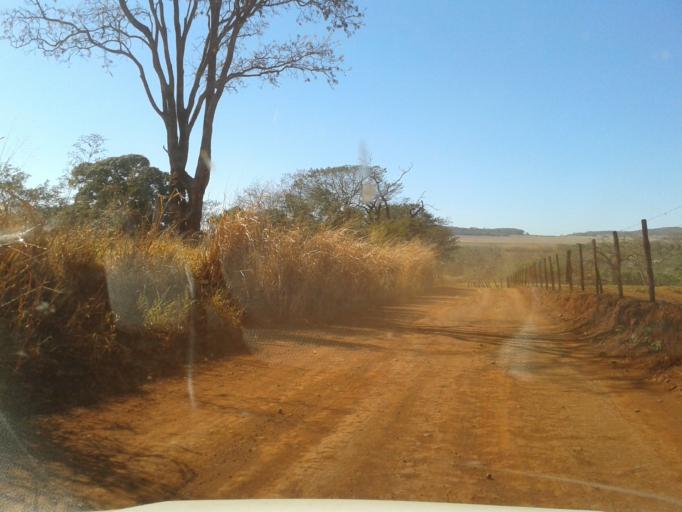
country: BR
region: Minas Gerais
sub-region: Centralina
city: Centralina
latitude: -18.5882
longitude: -49.1813
